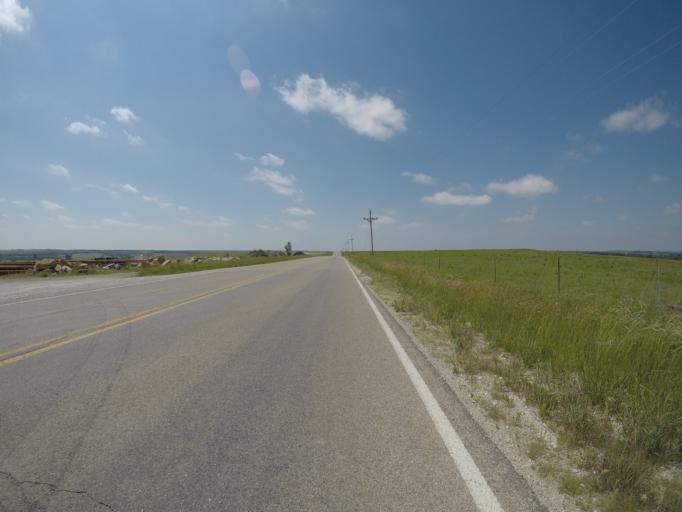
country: US
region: Kansas
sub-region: Pottawatomie County
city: Westmoreland
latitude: 39.3889
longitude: -96.4265
